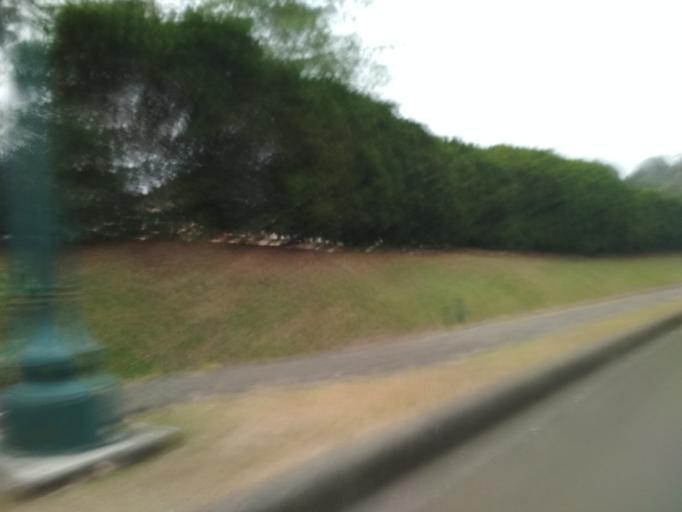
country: ID
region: West Java
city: Caringin
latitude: -6.6626
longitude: 106.8330
